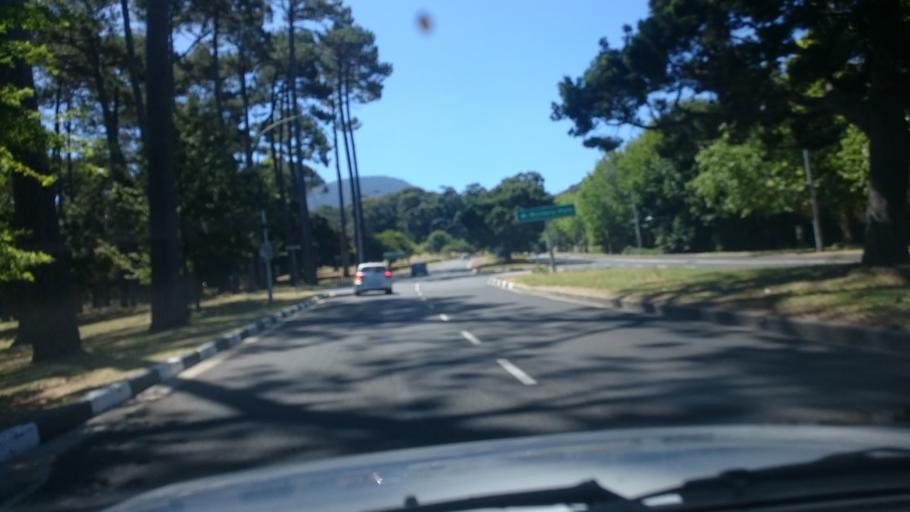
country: ZA
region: Western Cape
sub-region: City of Cape Town
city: Newlands
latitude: -33.9993
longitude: 18.4542
